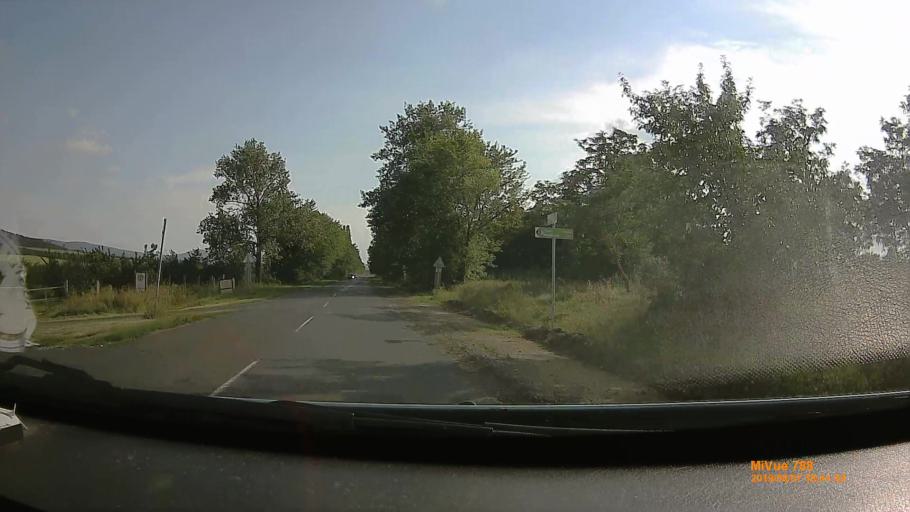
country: HU
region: Borsod-Abauj-Zemplen
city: Abaujszanto
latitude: 48.3478
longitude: 21.2109
